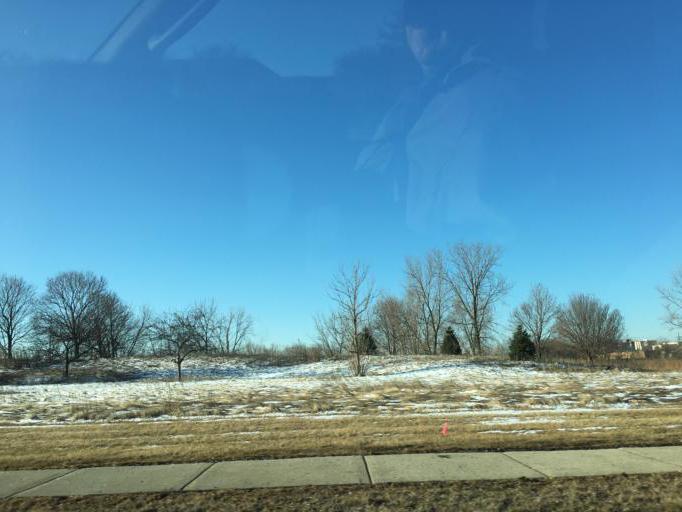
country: US
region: Illinois
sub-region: Cook County
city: Hoffman Estates
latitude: 42.0720
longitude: -88.0553
